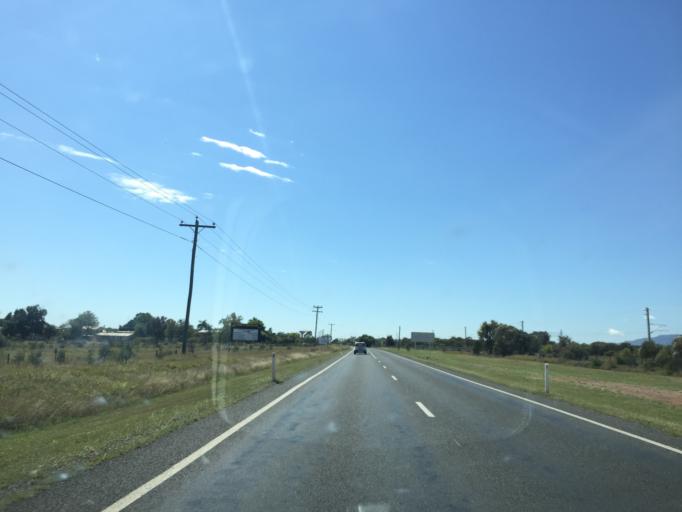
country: AU
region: Queensland
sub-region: Central Highlands
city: Blackwater
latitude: -23.5856
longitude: 148.8670
